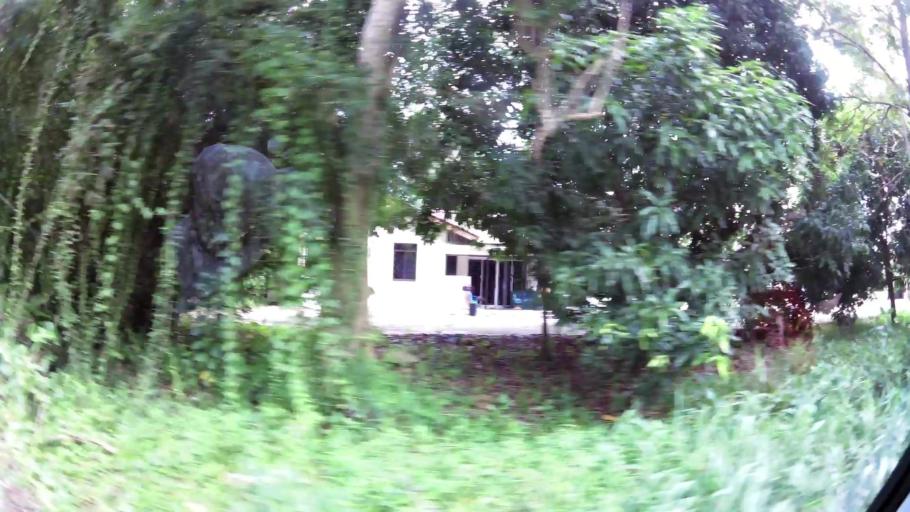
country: BN
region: Brunei and Muara
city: Bandar Seri Begawan
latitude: 4.9470
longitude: 114.9562
